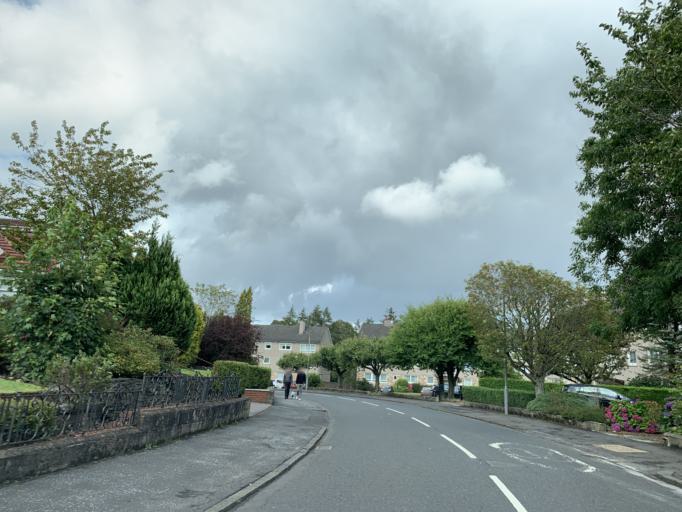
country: GB
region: Scotland
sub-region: East Renfrewshire
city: Newton Mearns
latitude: 55.7802
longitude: -4.3245
